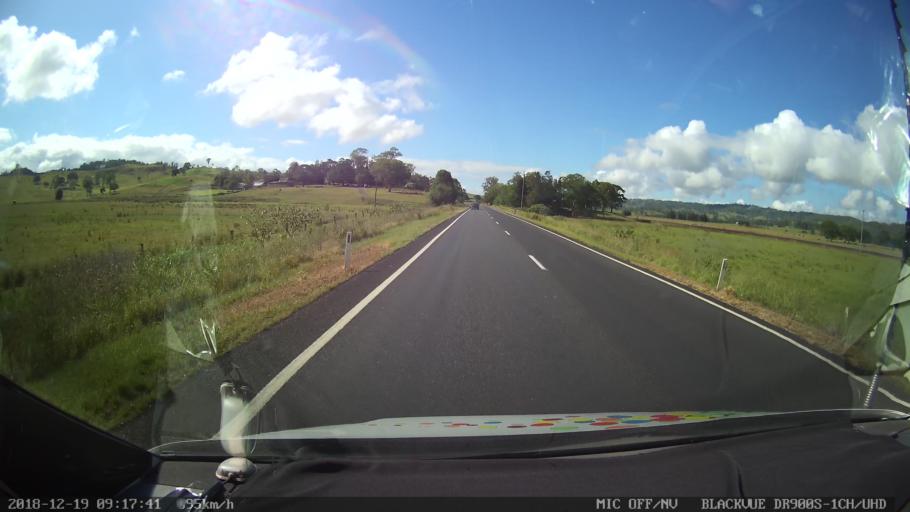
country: AU
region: New South Wales
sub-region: Kyogle
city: Kyogle
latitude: -28.5372
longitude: 152.9750
